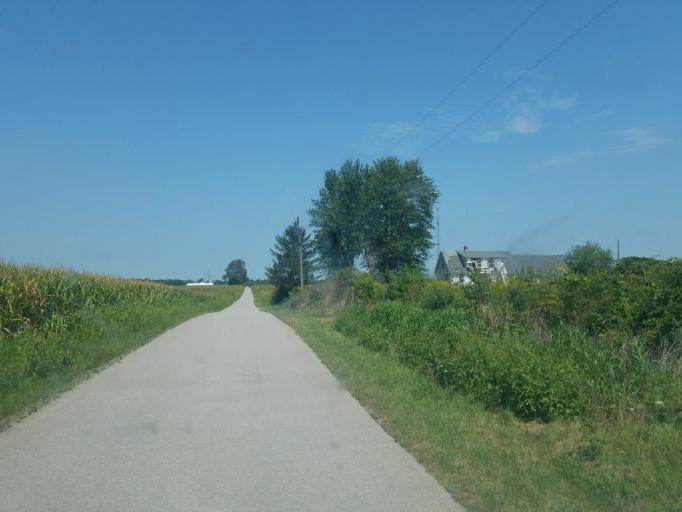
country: US
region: Ohio
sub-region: Crawford County
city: Bucyrus
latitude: 40.7767
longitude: -83.1118
